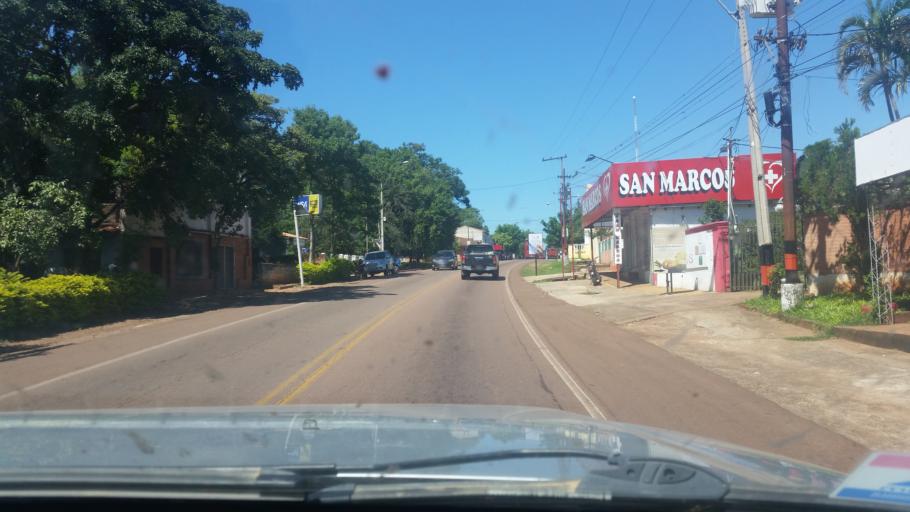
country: PY
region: Paraguari
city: Quiindy
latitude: -25.8778
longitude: -57.2896
